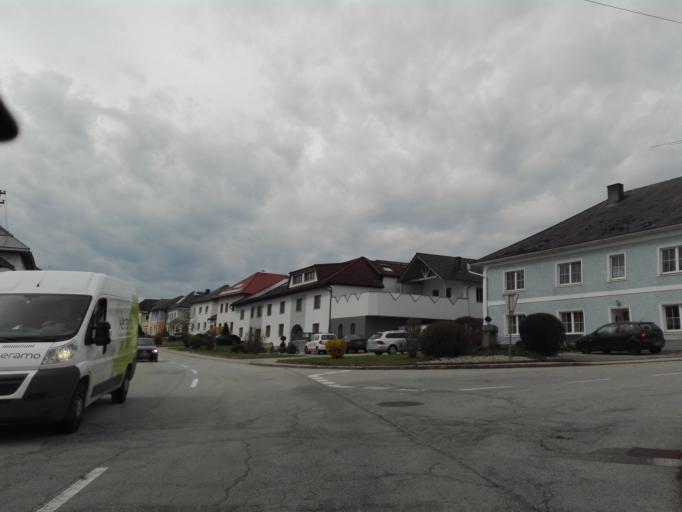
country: AT
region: Upper Austria
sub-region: Politischer Bezirk Rohrbach
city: Ulrichsberg
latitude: 48.6867
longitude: 13.9011
